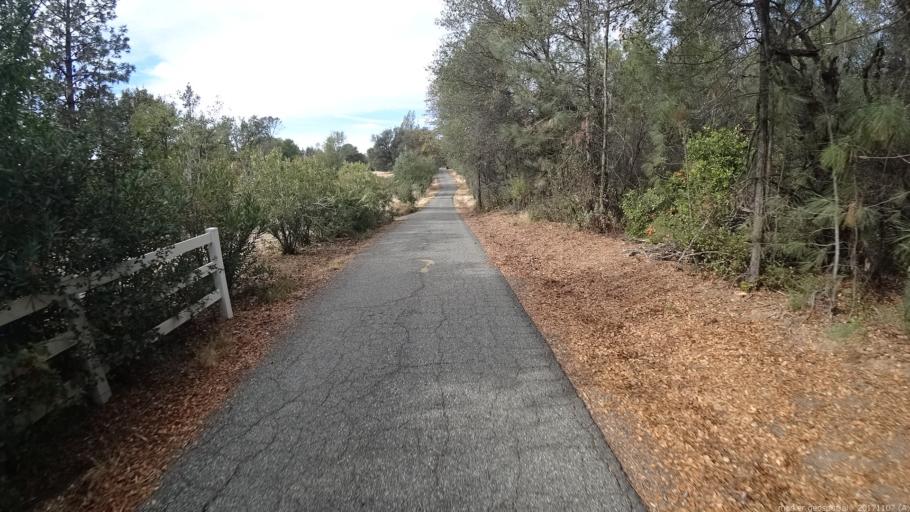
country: US
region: California
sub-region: Shasta County
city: Shasta
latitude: 40.5012
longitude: -122.5926
